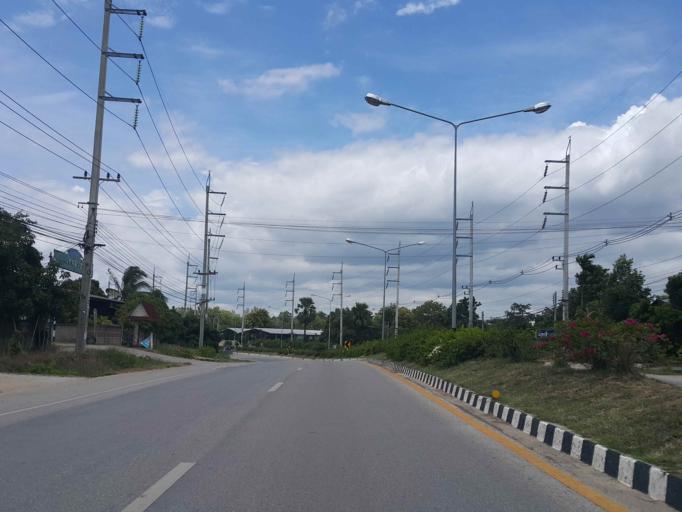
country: TH
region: Lamphun
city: Ban Hong
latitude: 18.3409
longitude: 98.8152
